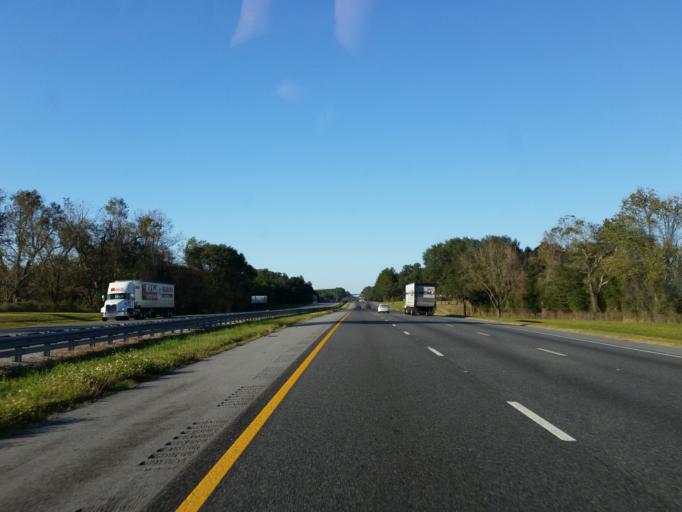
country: US
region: Florida
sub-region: Alachua County
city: High Springs
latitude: 30.0088
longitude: -82.6050
